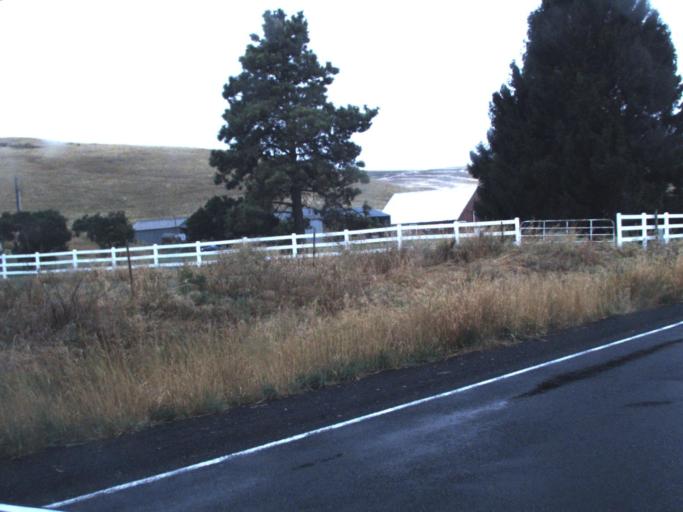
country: US
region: Washington
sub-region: Whitman County
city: Colfax
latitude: 47.0114
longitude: -117.4763
